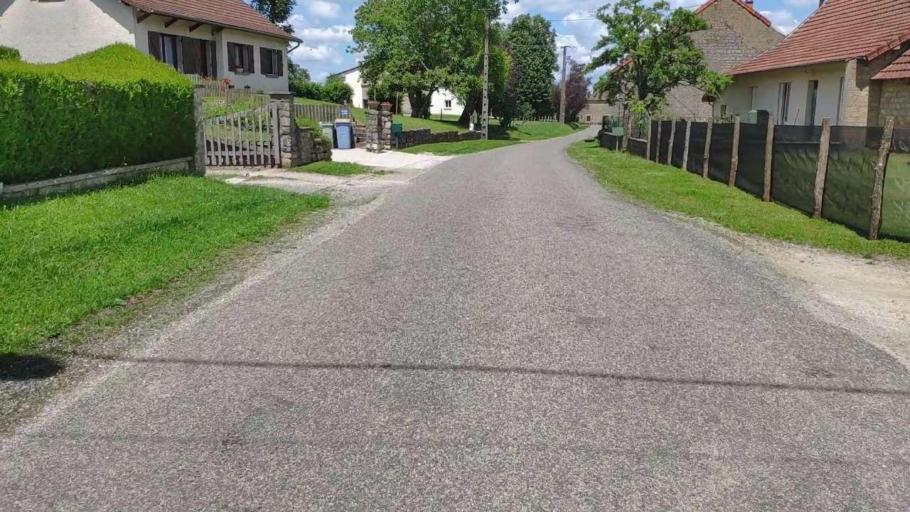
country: FR
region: Franche-Comte
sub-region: Departement du Jura
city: Bletterans
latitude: 46.8451
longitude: 5.4725
